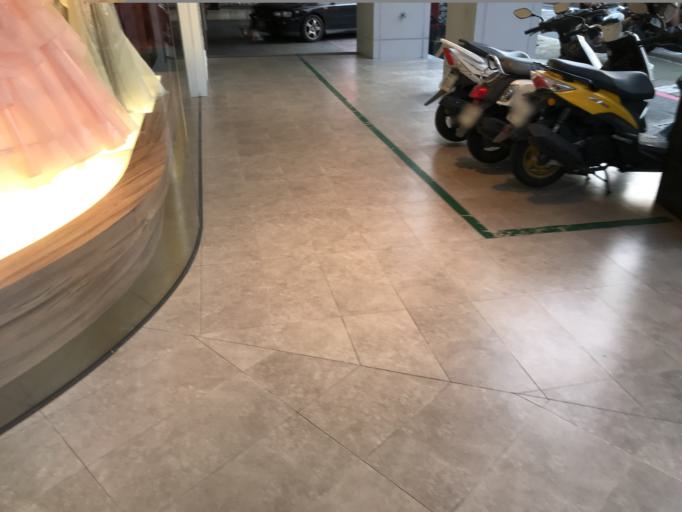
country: TW
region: Taiwan
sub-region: Tainan
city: Tainan
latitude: 22.9928
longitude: 120.2056
